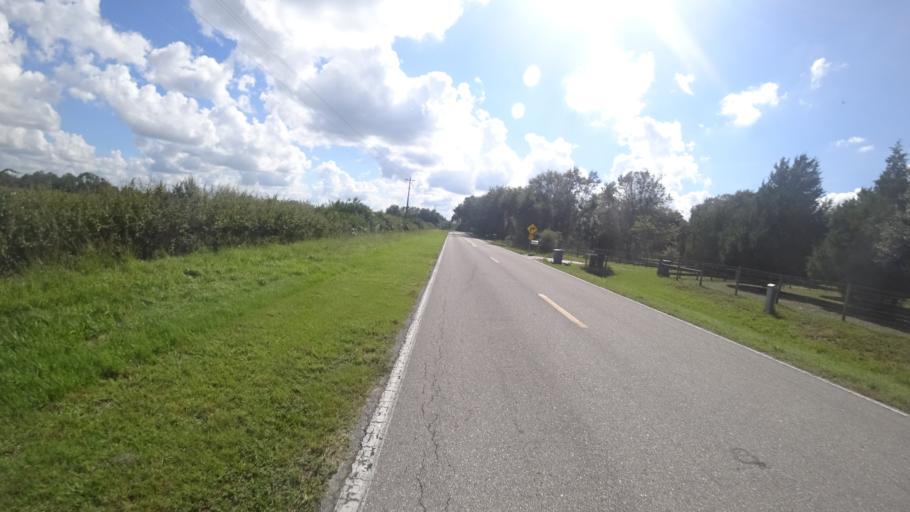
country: US
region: Florida
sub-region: Sarasota County
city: Lake Sarasota
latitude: 27.3700
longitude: -82.1412
